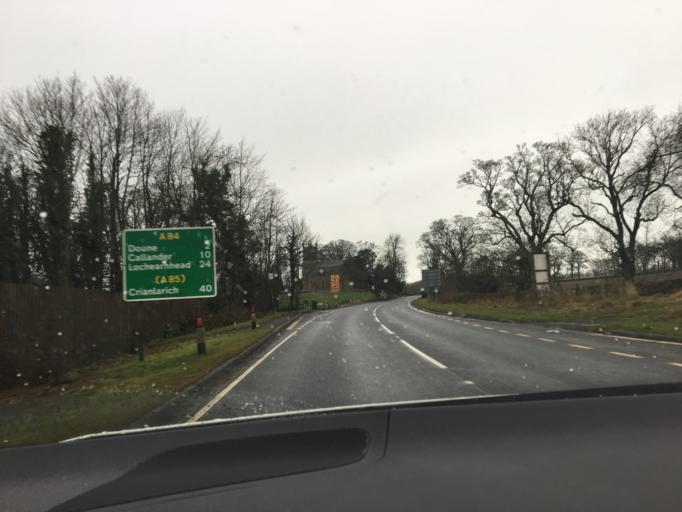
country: GB
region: Scotland
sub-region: Stirling
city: Doune
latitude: 56.1634
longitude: -4.0617
